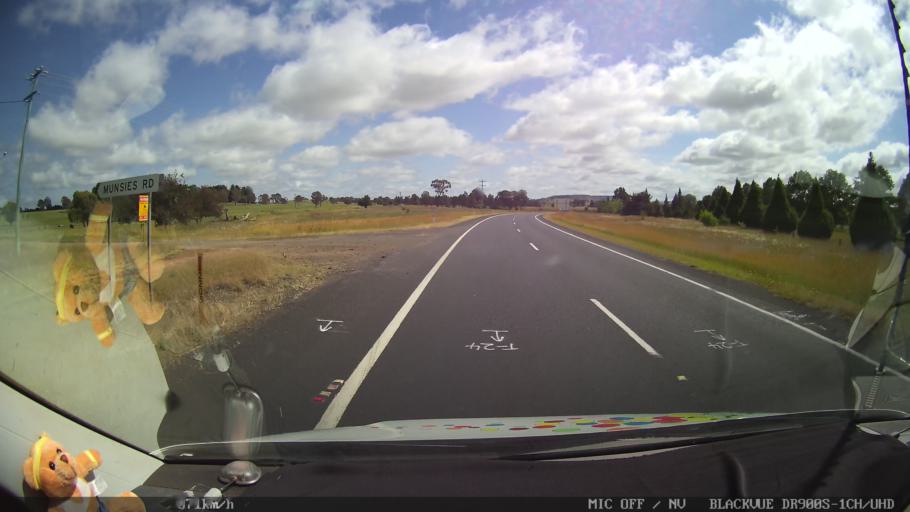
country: AU
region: New South Wales
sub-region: Glen Innes Severn
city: Glen Innes
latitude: -29.9211
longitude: 151.7250
